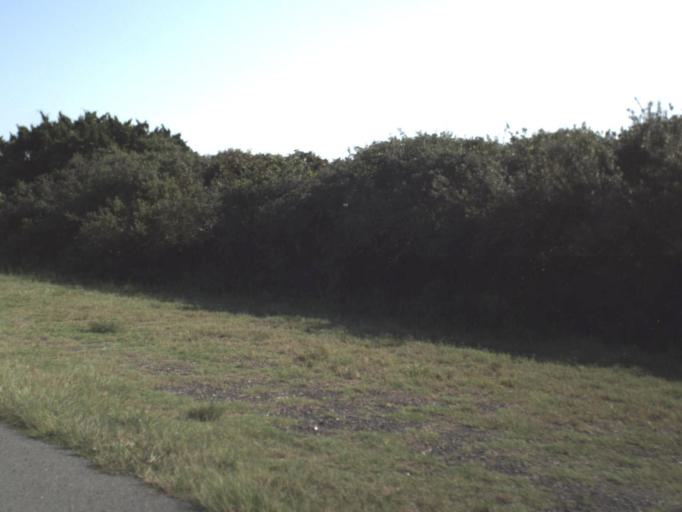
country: US
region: Florida
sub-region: Saint Johns County
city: Butler Beach
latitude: 29.7000
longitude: -81.2264
